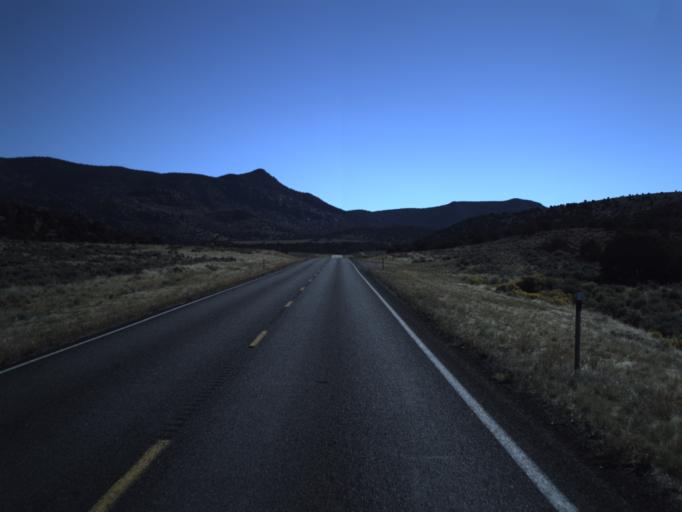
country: US
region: Utah
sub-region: Washington County
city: Enterprise
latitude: 37.6757
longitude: -113.5083
